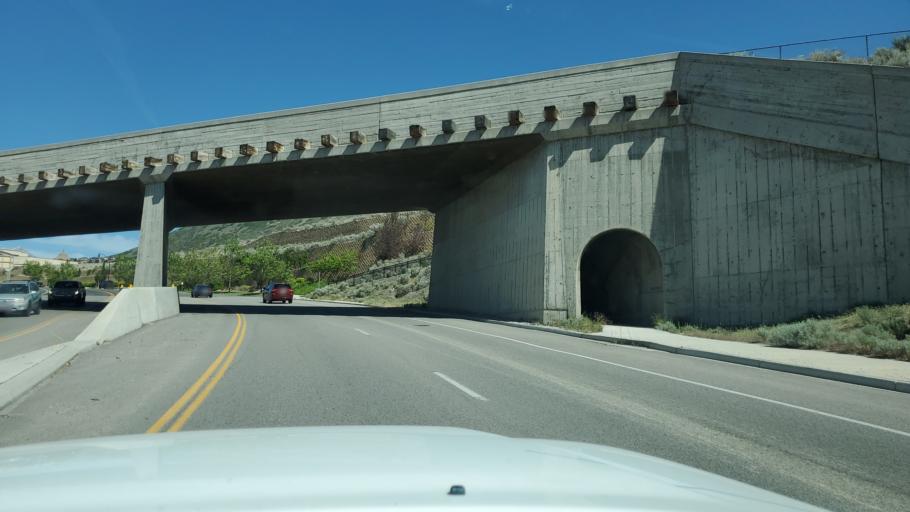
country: US
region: Utah
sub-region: Salt Lake County
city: Bluffdale
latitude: 40.4821
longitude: -111.8961
